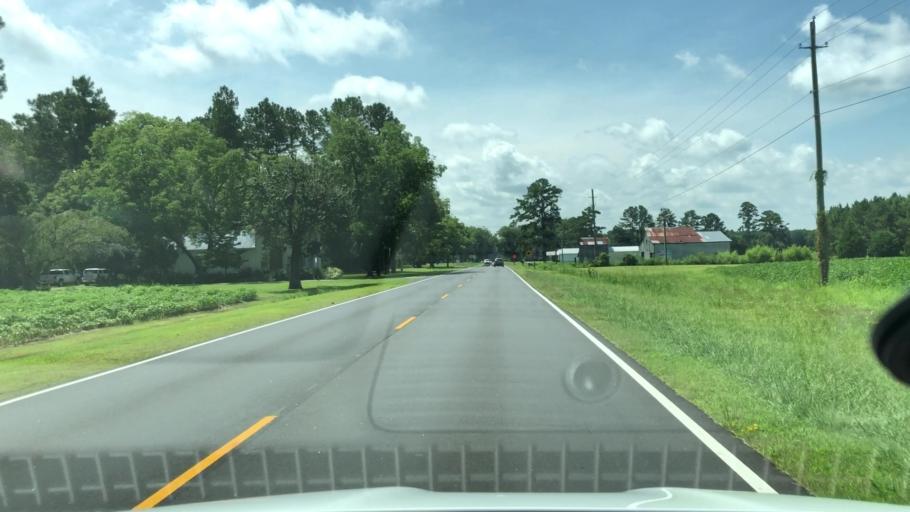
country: US
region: North Carolina
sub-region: Martin County
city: Williamston
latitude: 35.7445
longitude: -77.0758
